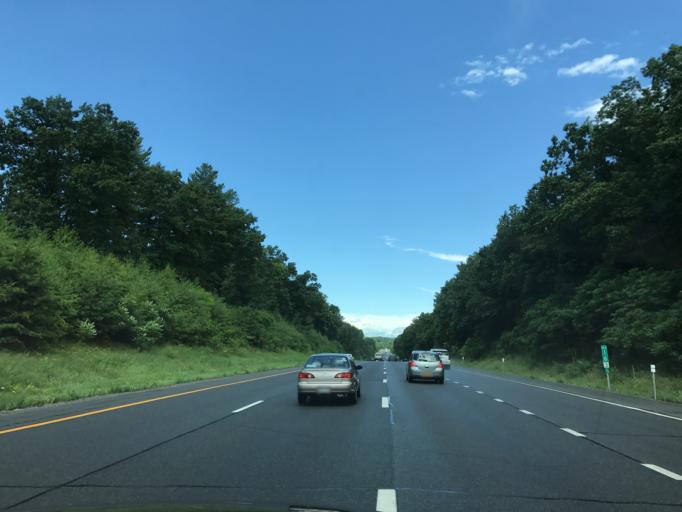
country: US
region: New York
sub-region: Saratoga County
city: Country Knolls
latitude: 42.9047
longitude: -73.7874
